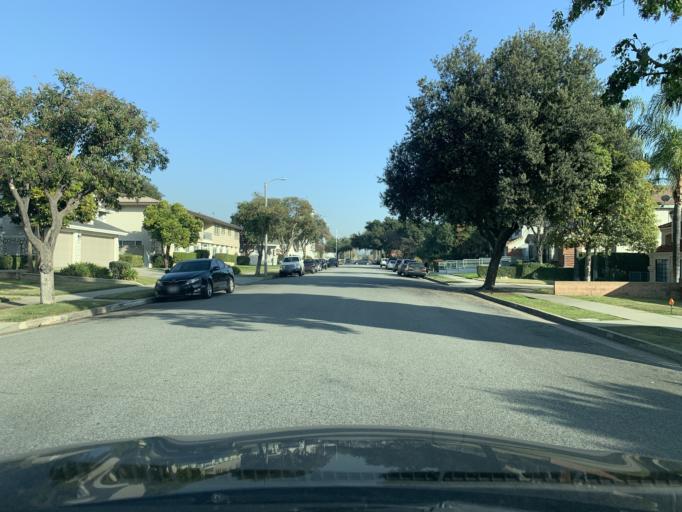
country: US
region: California
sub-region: Los Angeles County
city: Covina
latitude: 34.0839
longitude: -117.8937
